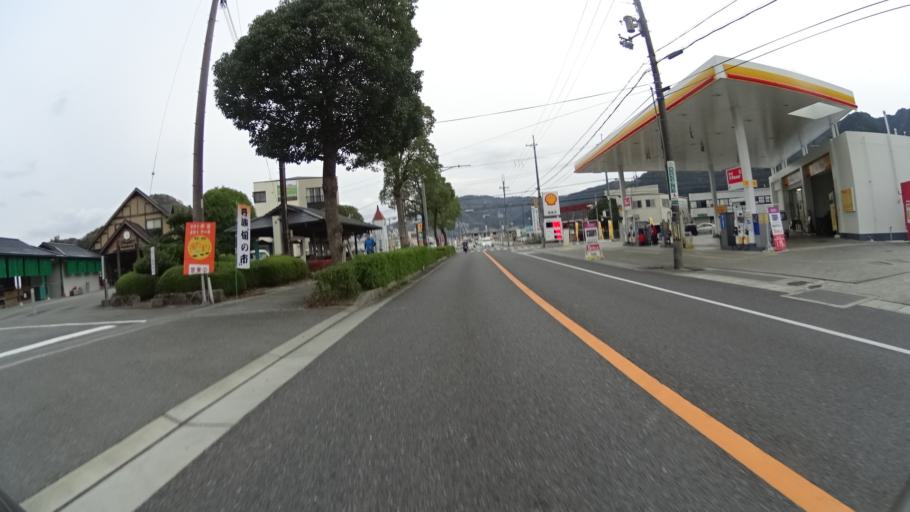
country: JP
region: Hyogo
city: Sasayama
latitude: 35.0644
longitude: 135.1899
